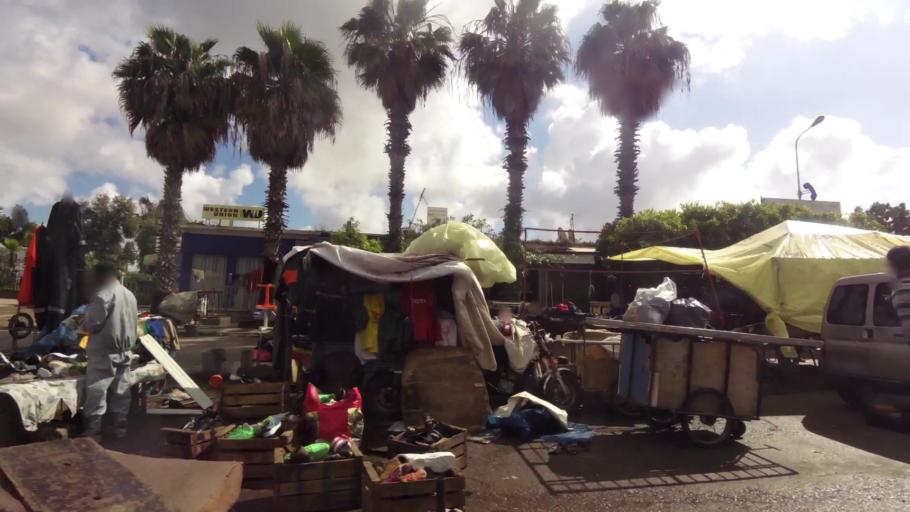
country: MA
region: Grand Casablanca
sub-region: Casablanca
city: Casablanca
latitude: 33.5331
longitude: -7.6701
